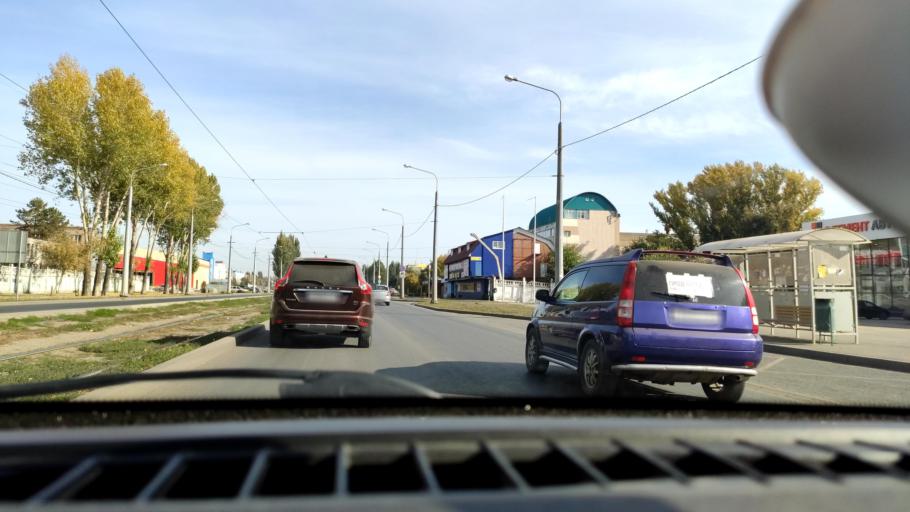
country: RU
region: Samara
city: Samara
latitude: 53.1992
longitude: 50.2569
